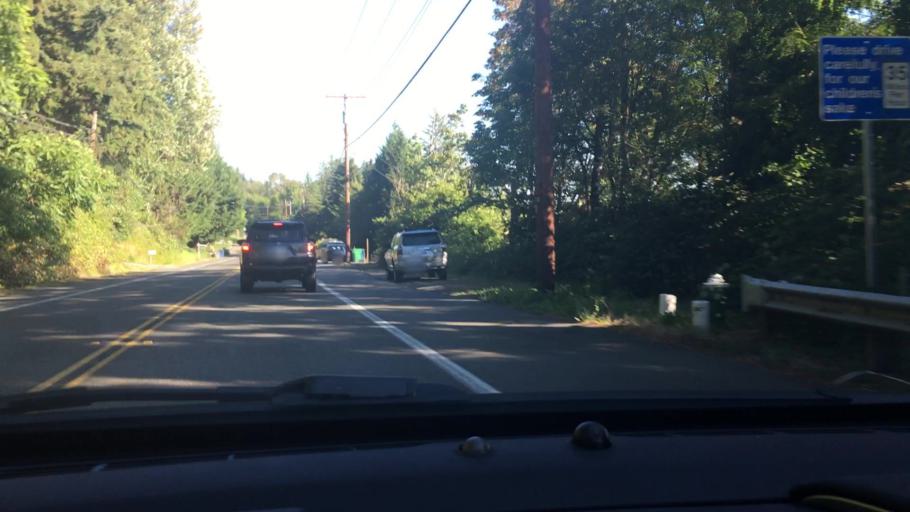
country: US
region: Washington
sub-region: King County
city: Sammamish
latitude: 47.6442
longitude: -122.0830
